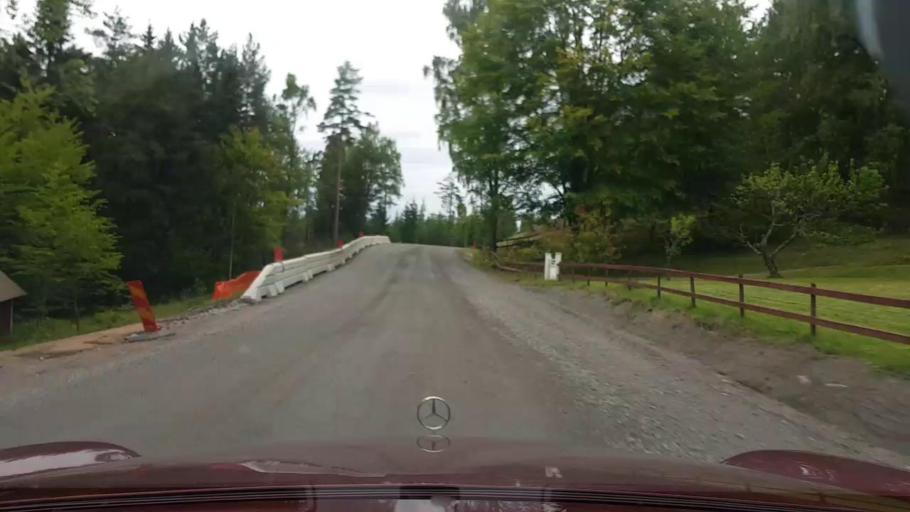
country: SE
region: Vaestra Goetaland
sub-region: Karlsborgs Kommun
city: Karlsborg
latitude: 58.7058
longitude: 14.5013
